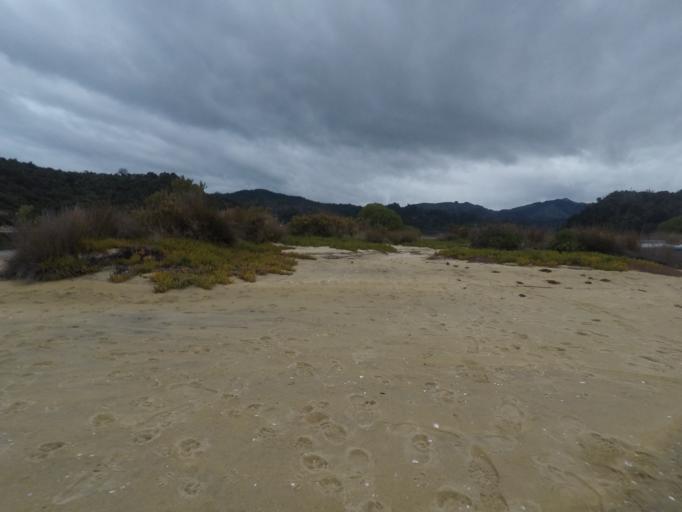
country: NZ
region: Tasman
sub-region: Tasman District
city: Motueka
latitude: -41.0125
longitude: 173.0065
